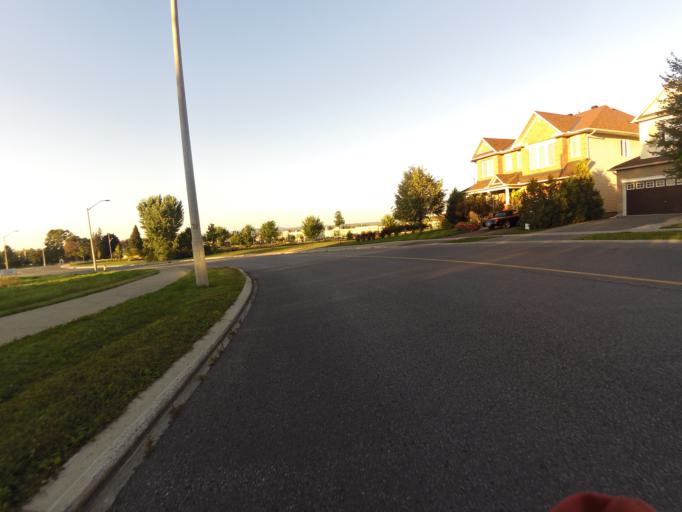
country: CA
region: Ontario
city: Bells Corners
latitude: 45.3563
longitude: -75.9375
